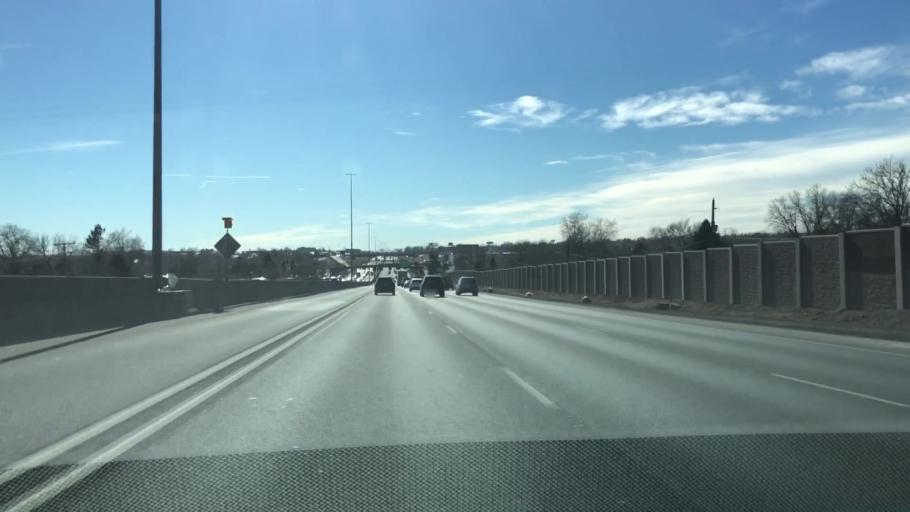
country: US
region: Colorado
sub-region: Adams County
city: Northglenn
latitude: 39.8951
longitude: -104.9882
